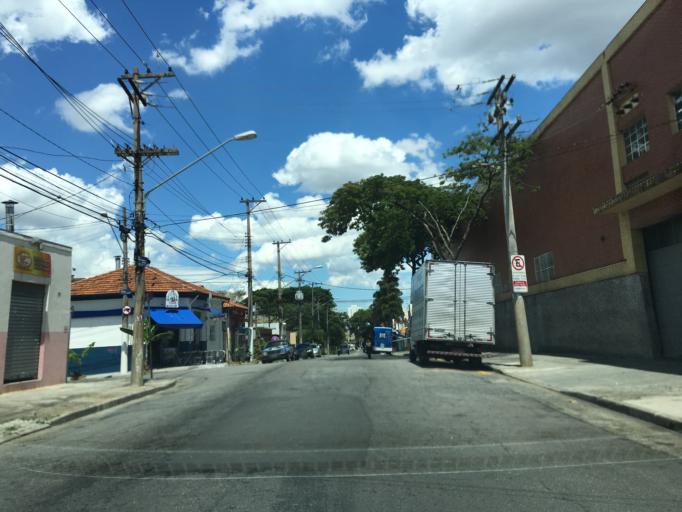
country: BR
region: Sao Paulo
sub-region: Sao Caetano Do Sul
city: Sao Caetano do Sul
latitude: -23.5714
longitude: -46.5661
